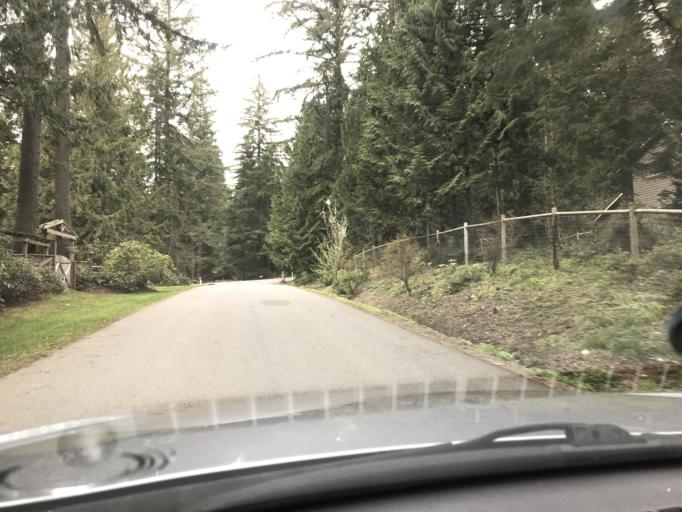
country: US
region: Washington
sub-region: King County
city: Union Hill-Novelty Hill
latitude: 47.6990
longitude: -122.0414
